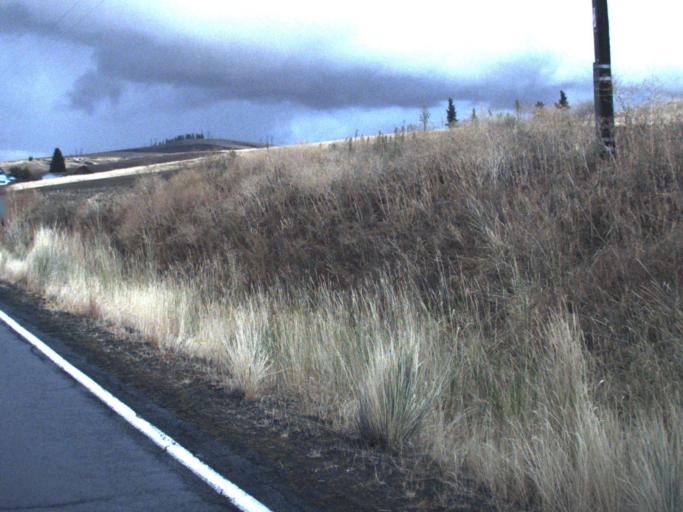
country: US
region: Washington
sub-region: Spokane County
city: Medical Lake
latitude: 47.7100
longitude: -117.8739
